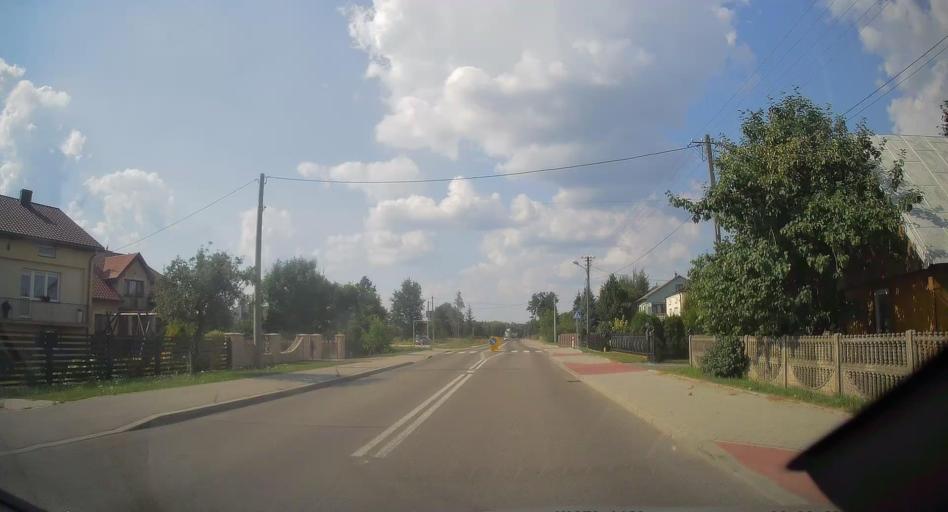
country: PL
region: Swietokrzyskie
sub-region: Powiat konecki
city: Radoszyce
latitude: 51.0522
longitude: 20.2808
